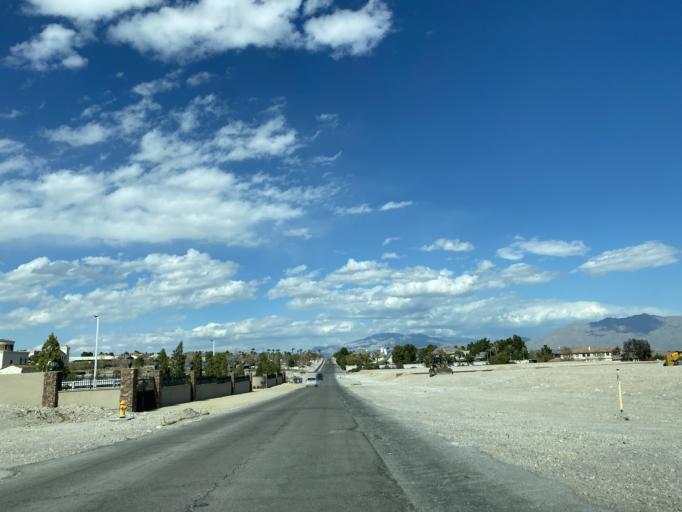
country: US
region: Nevada
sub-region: Clark County
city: Summerlin South
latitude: 36.2366
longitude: -115.3088
